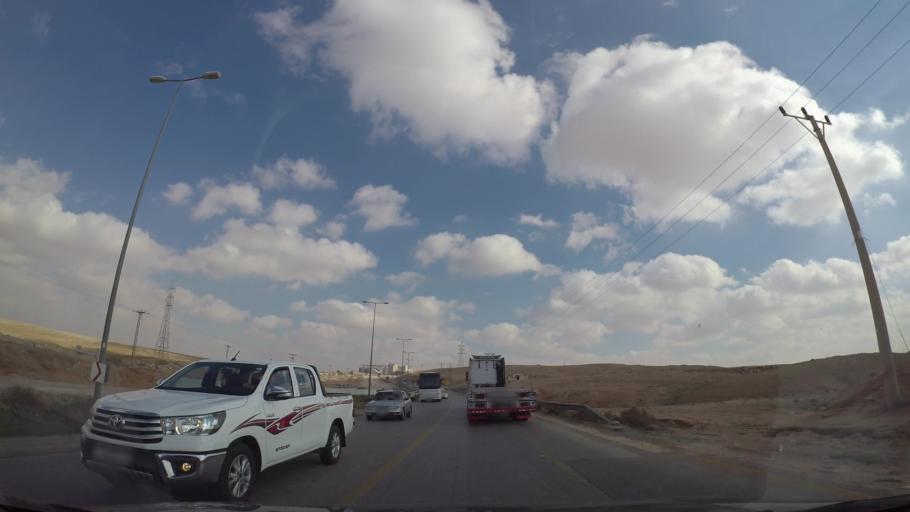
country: JO
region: Amman
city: Al Jizah
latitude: 31.6293
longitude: 35.9870
